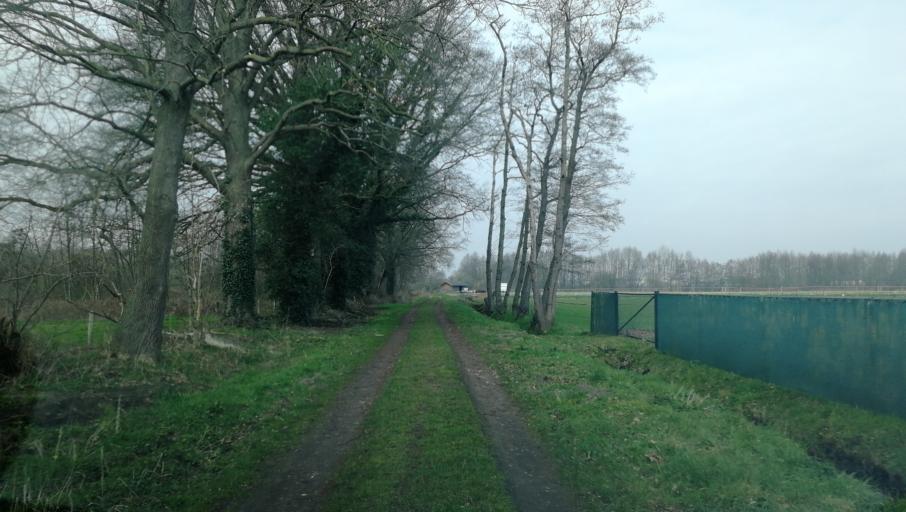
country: NL
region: Limburg
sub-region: Gemeente Peel en Maas
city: Maasbree
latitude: 51.4376
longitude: 6.0635
